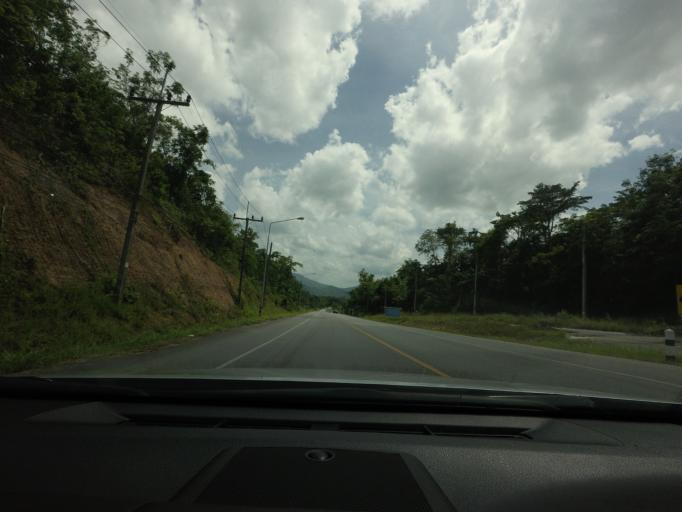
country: TH
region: Yala
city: Raman
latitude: 6.4666
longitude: 101.3866
